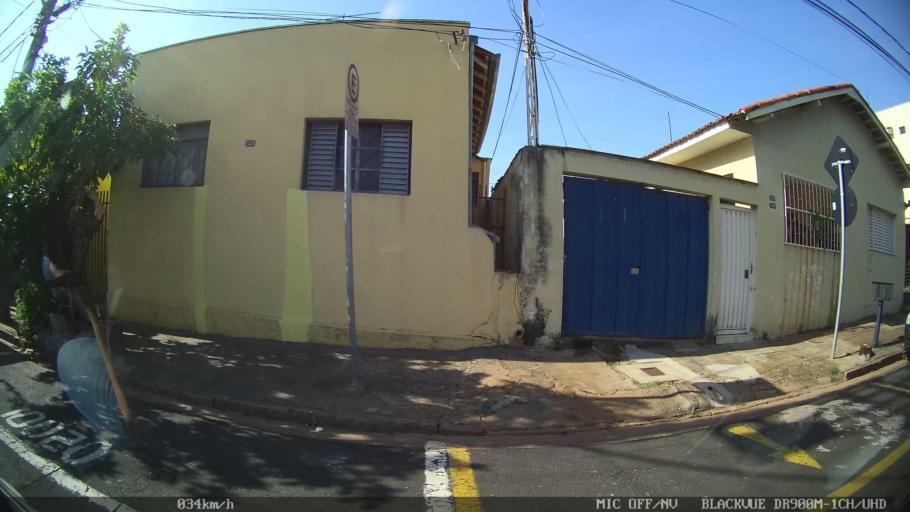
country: BR
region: Sao Paulo
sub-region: Sao Jose Do Rio Preto
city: Sao Jose do Rio Preto
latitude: -20.8203
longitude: -49.3780
